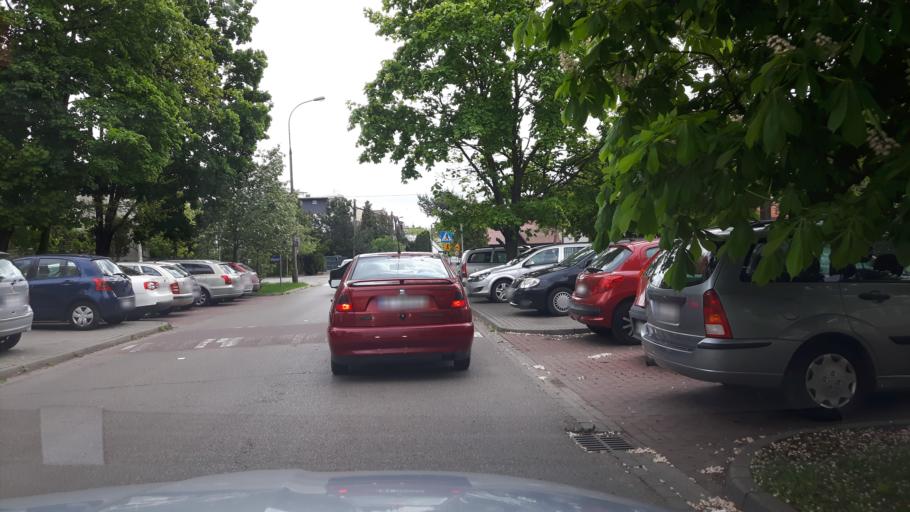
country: PL
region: Masovian Voivodeship
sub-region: Warszawa
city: Rembertow
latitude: 52.2374
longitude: 21.1493
